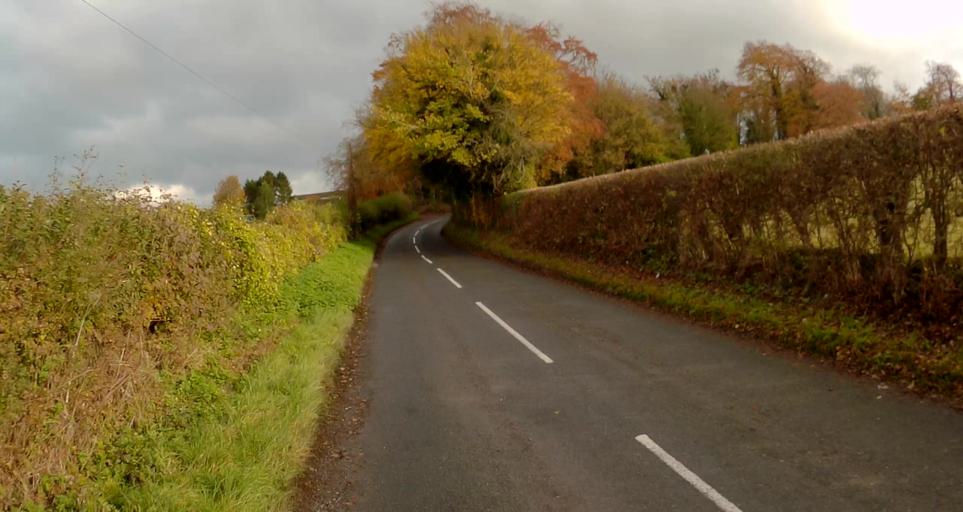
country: GB
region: England
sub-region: Hampshire
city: Old Basing
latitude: 51.2466
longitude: -1.0418
